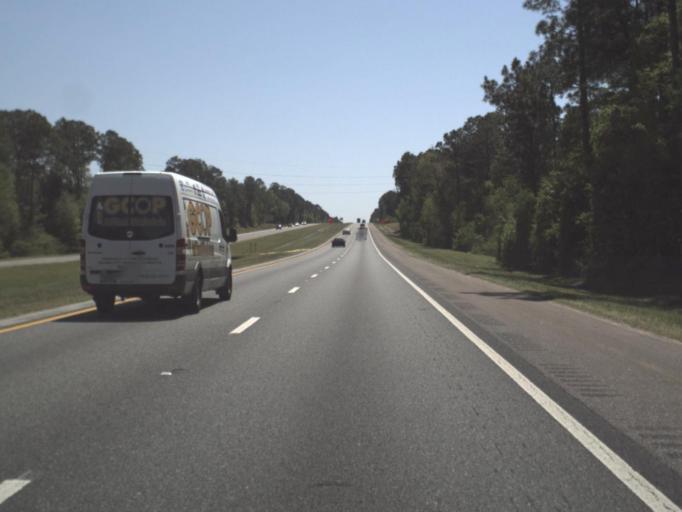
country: US
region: Florida
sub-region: Escambia County
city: Ensley
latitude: 30.5159
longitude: -87.3035
